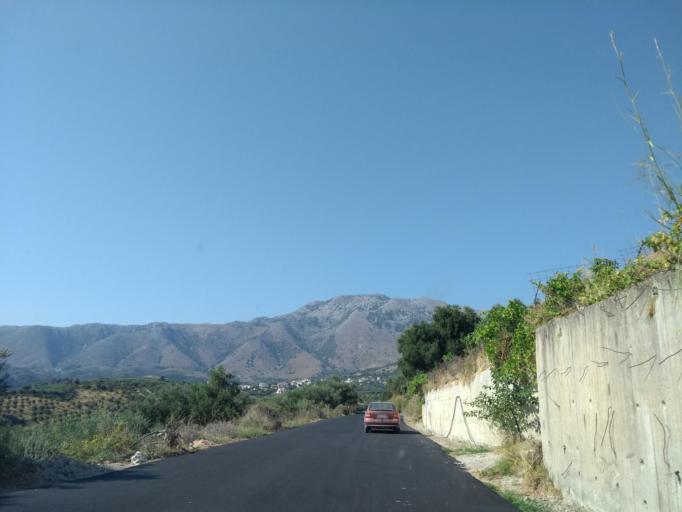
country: GR
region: Crete
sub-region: Nomos Chanias
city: Georgioupolis
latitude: 35.3313
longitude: 24.3013
